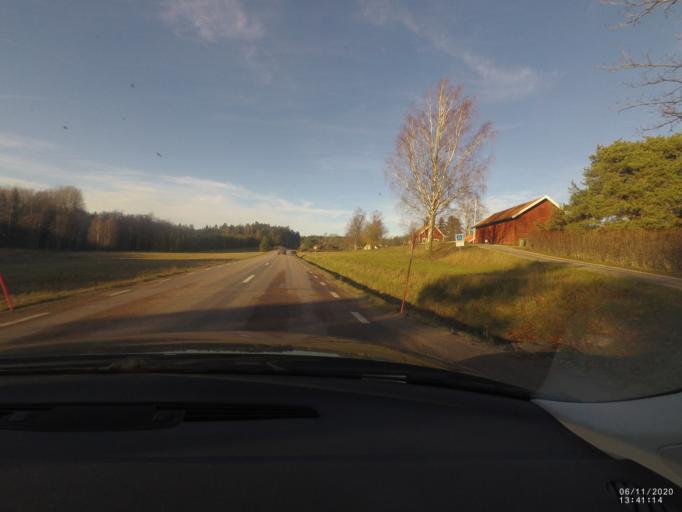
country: SE
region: Soedermanland
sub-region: Nykopings Kommun
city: Nykoping
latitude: 58.8350
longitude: 17.0730
